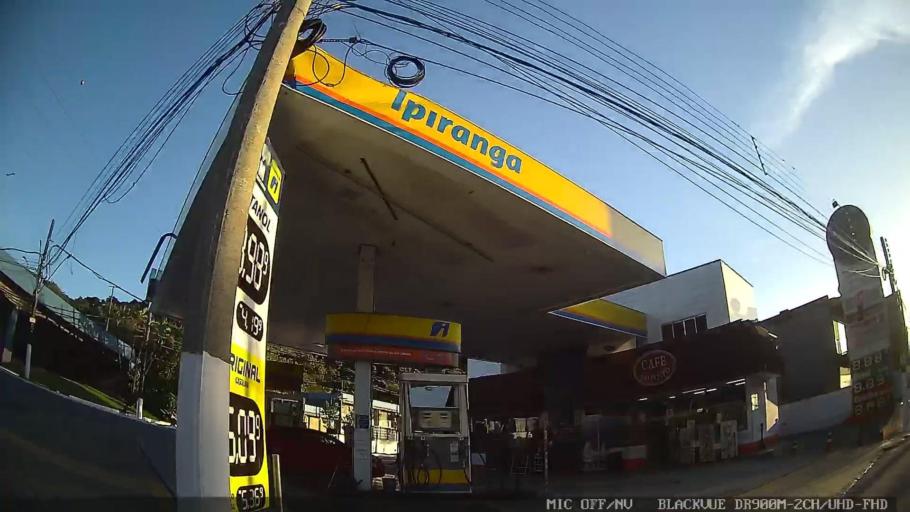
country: BR
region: Sao Paulo
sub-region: Guaruja
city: Guaruja
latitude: -23.9895
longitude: -46.2599
